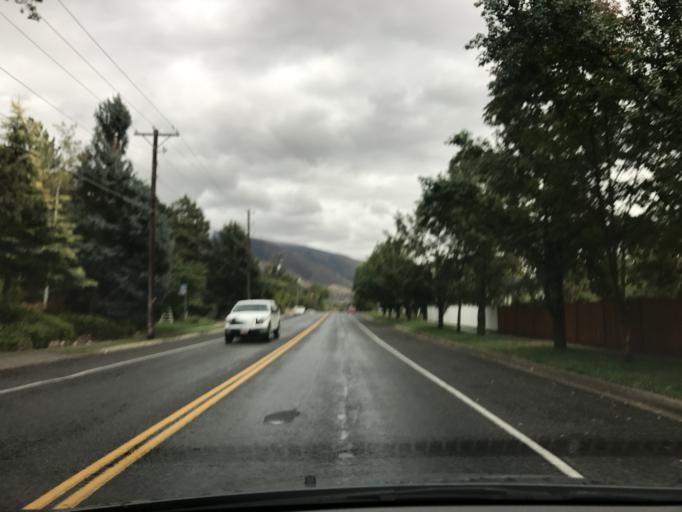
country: US
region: Utah
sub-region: Davis County
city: Fruit Heights
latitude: 41.0050
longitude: -111.9047
